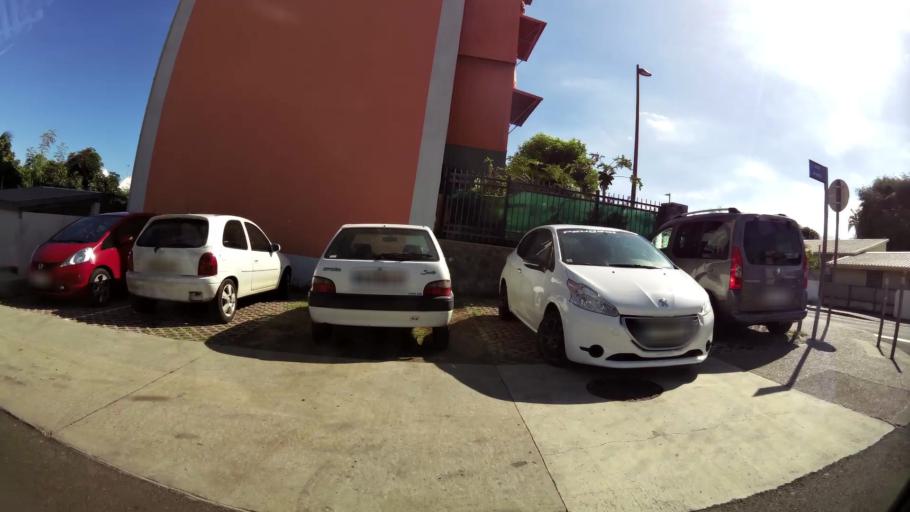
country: RE
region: Reunion
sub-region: Reunion
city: Saint-Pierre
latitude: -21.3360
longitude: 55.4610
